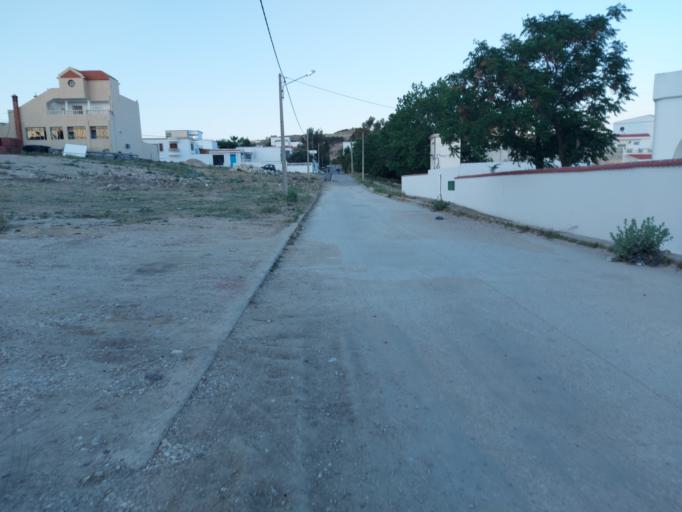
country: TN
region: Kef
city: El Kef
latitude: 36.1806
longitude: 8.7282
